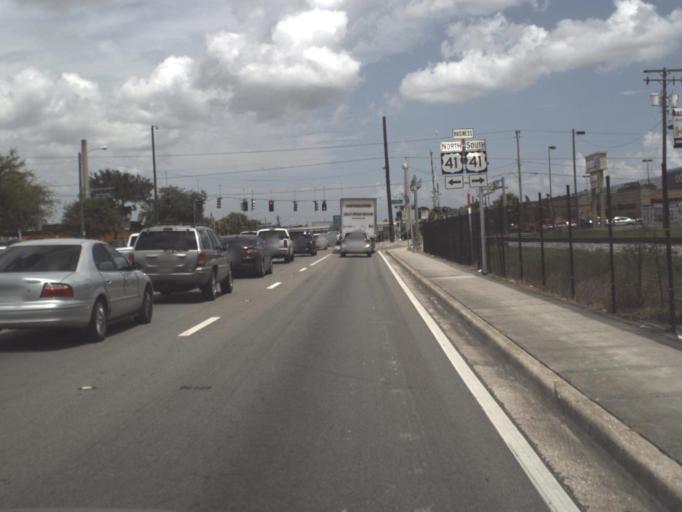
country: US
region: Florida
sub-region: Hillsborough County
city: Carrollwood
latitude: 28.0329
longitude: -82.4607
